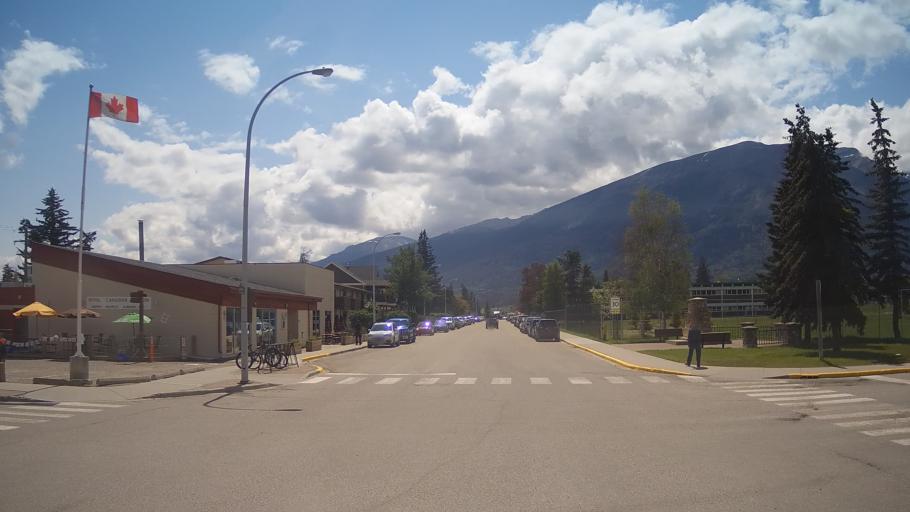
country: CA
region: Alberta
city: Jasper Park Lodge
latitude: 52.8796
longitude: -118.0818
